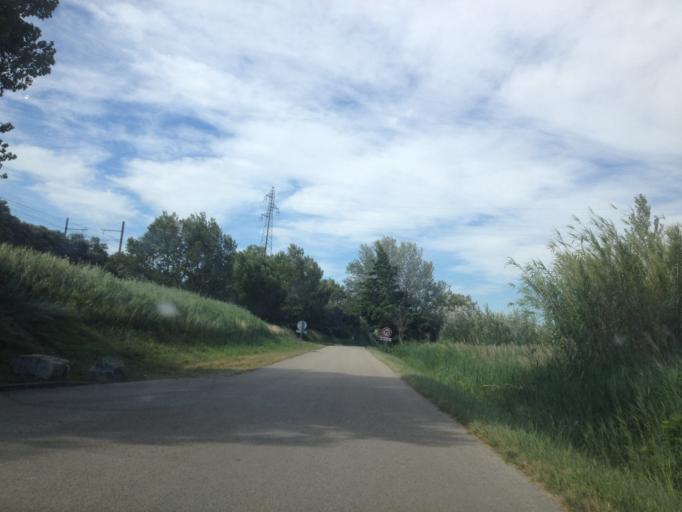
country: FR
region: Provence-Alpes-Cote d'Azur
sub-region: Departement du Vaucluse
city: Sorgues
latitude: 44.0226
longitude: 4.8814
